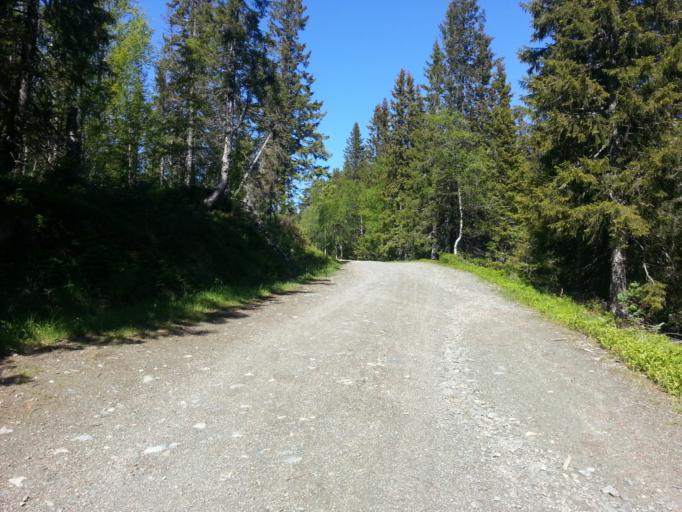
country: NO
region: Sor-Trondelag
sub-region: Trondheim
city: Trondheim
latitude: 63.4086
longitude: 10.2888
